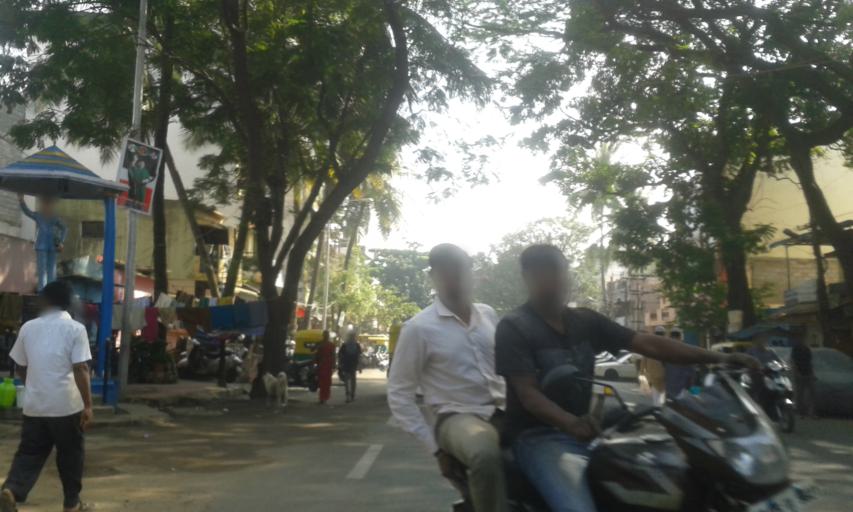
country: IN
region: Karnataka
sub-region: Bangalore Urban
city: Bangalore
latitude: 12.9285
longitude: 77.5953
